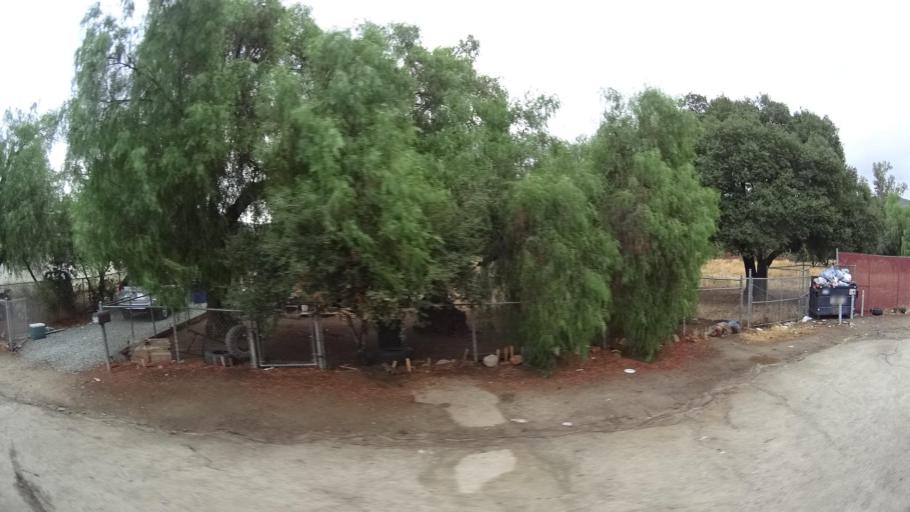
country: MX
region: Baja California
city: Tecate
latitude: 32.5815
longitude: -116.6213
